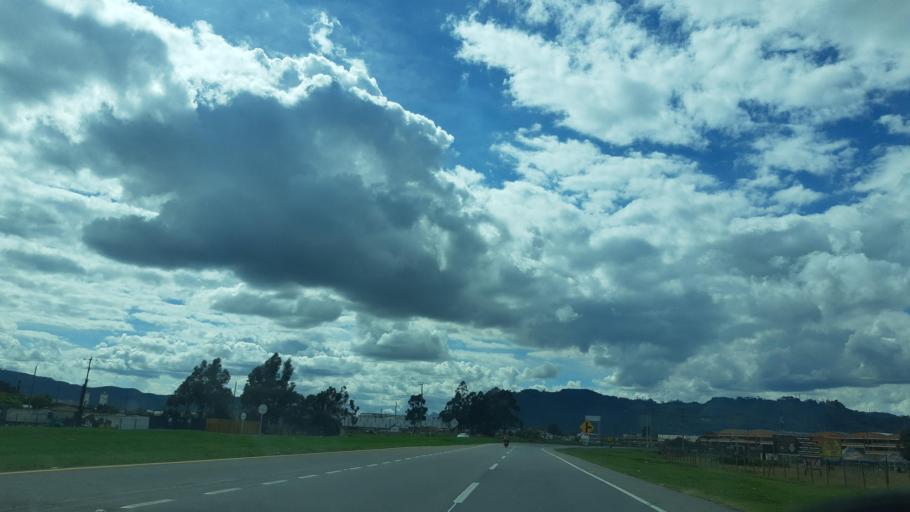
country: CO
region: Cundinamarca
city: Tocancipa
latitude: 4.9522
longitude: -73.9335
